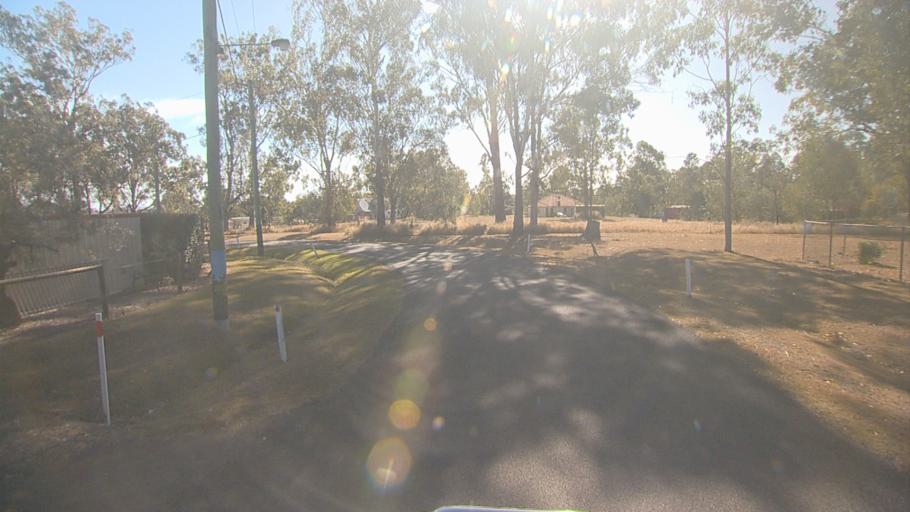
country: AU
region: Queensland
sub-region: Logan
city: Cedar Vale
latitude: -27.8586
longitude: 152.9826
